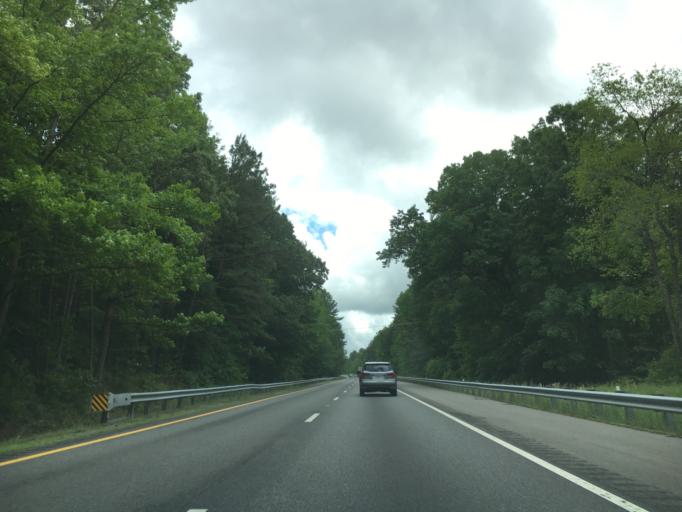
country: US
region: Virginia
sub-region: Mecklenburg County
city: South Hill
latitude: 36.7252
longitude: -78.1080
